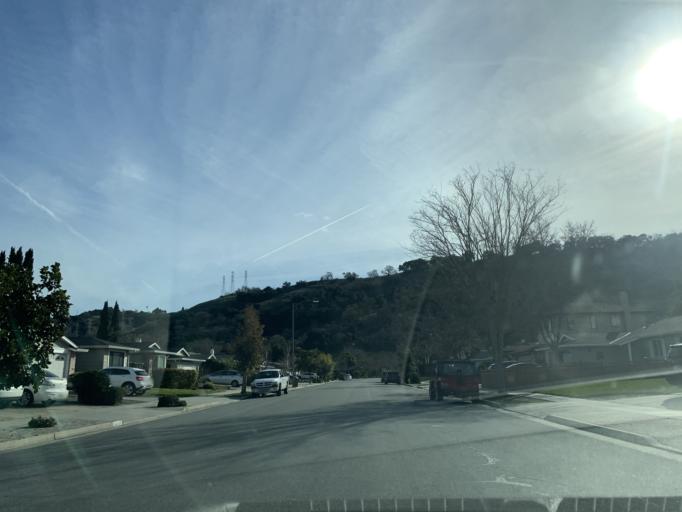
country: US
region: California
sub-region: Santa Clara County
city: Seven Trees
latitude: 37.2332
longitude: -121.8409
